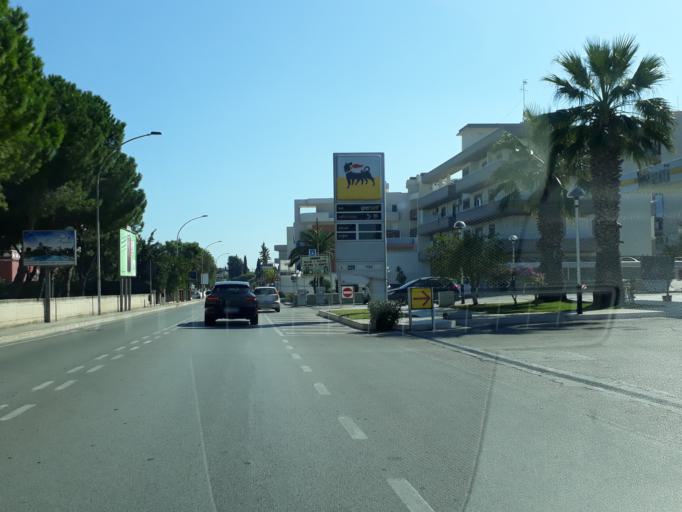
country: IT
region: Apulia
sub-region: Provincia di Bari
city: Monopoli
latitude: 40.9479
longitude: 17.2913
